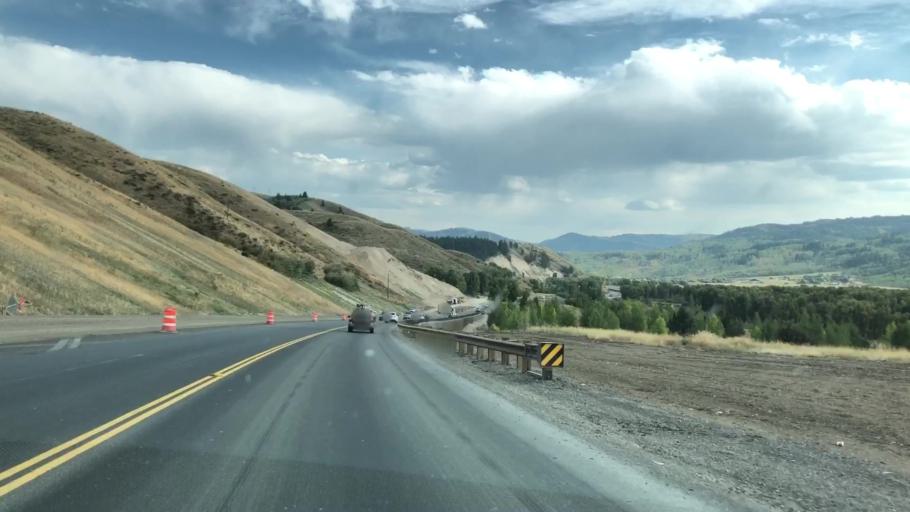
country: US
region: Wyoming
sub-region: Teton County
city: South Park
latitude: 43.3989
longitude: -110.7510
